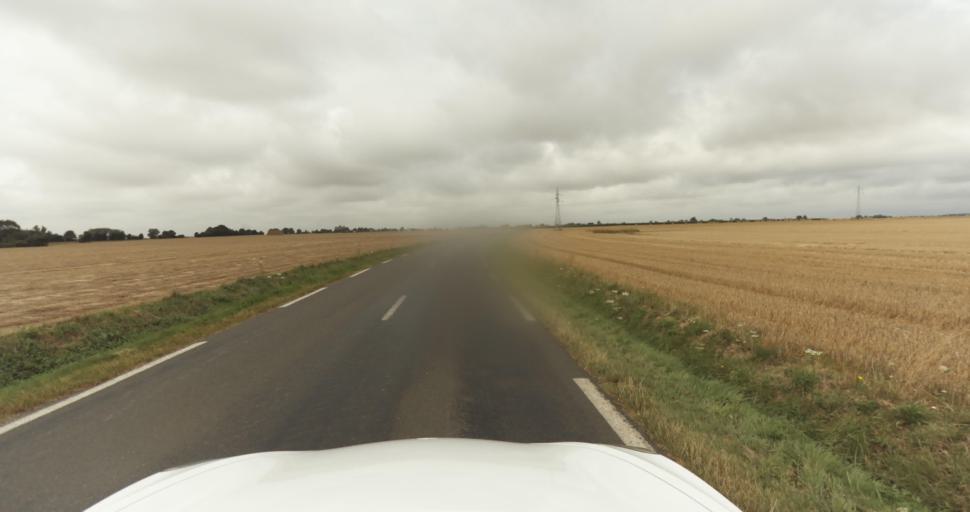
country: FR
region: Haute-Normandie
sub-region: Departement de l'Eure
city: Claville
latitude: 49.0806
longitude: 1.0556
